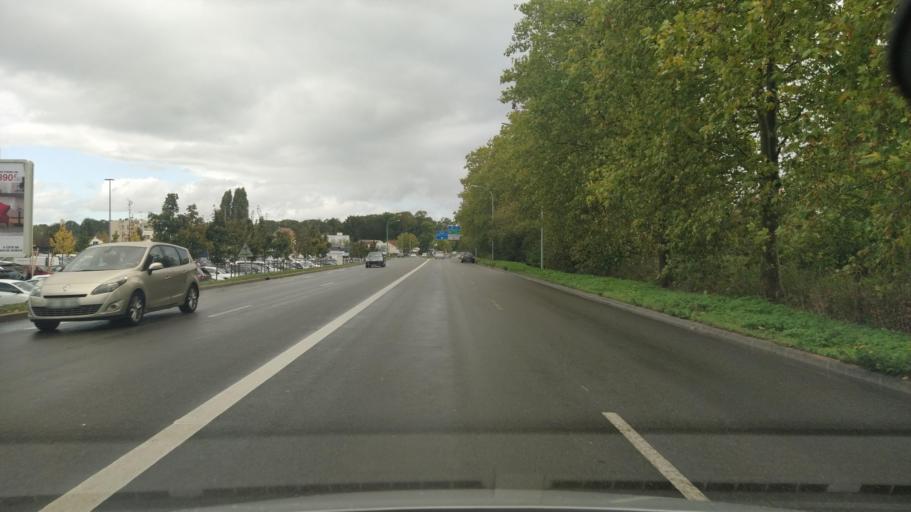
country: FR
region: Ile-de-France
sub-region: Departement des Yvelines
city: Bois-d'Arcy
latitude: 48.7985
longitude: 2.0387
